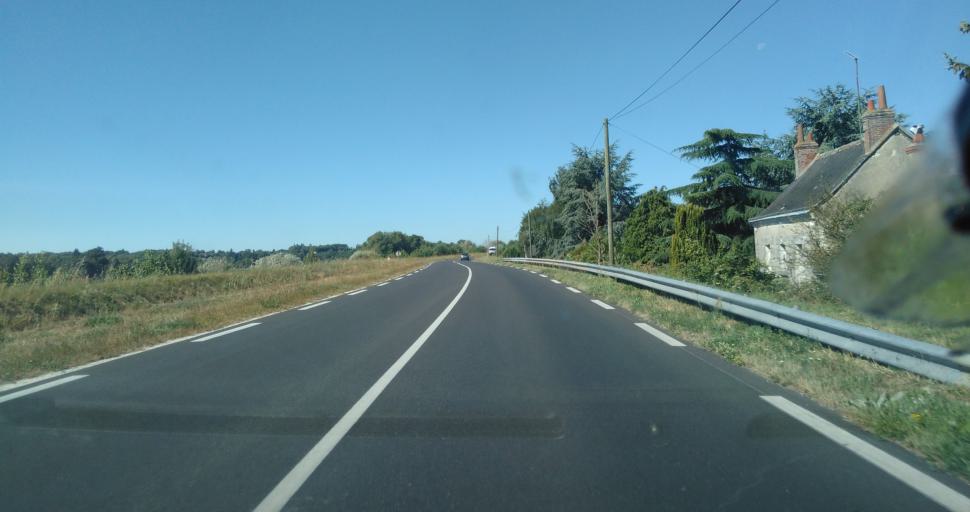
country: FR
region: Centre
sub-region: Departement d'Indre-et-Loire
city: Nazelles-Negron
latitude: 47.4067
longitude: 0.9404
